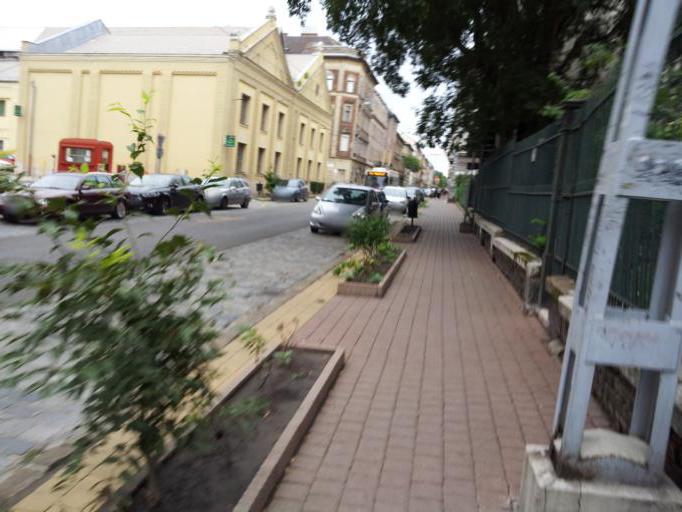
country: HU
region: Budapest
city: Budapest VII. keruelet
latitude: 47.5048
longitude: 19.0769
